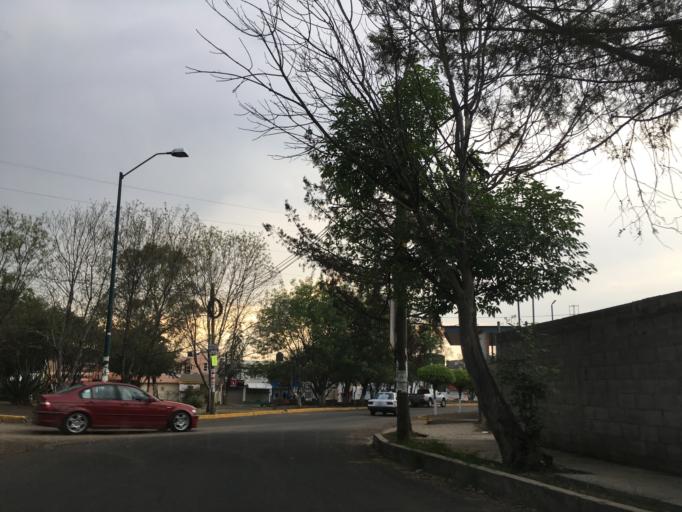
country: MX
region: Michoacan
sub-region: Morelia
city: Puerto de Buenavista (Lazaro Cardenas)
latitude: 19.6848
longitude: -101.1518
